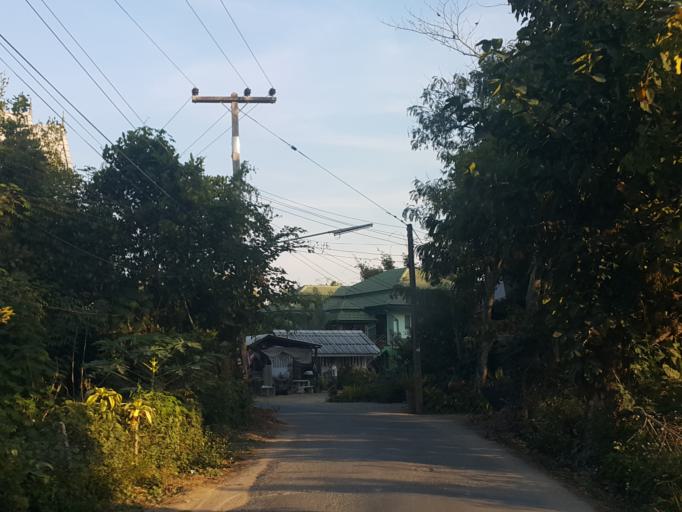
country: TH
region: Chiang Mai
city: San Sai
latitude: 18.8214
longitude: 99.0909
